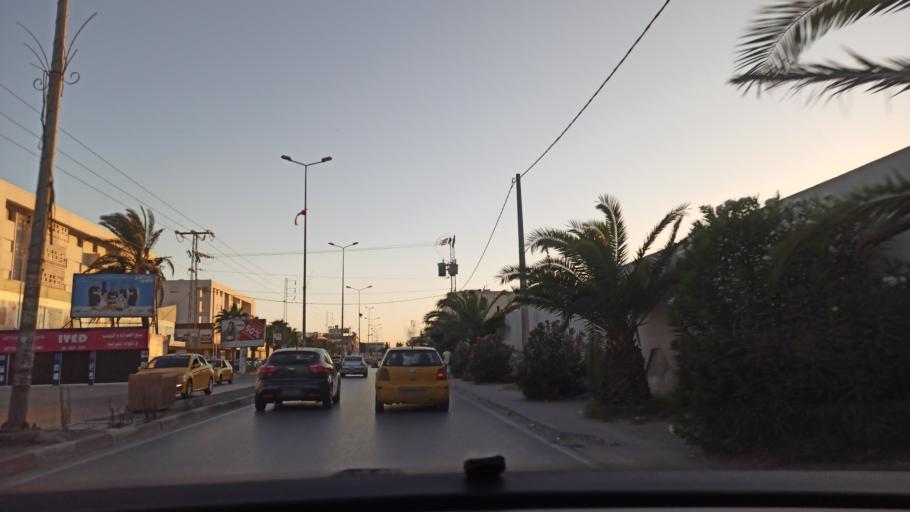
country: TN
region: Ariana
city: Ariana
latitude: 36.8614
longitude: 10.2099
